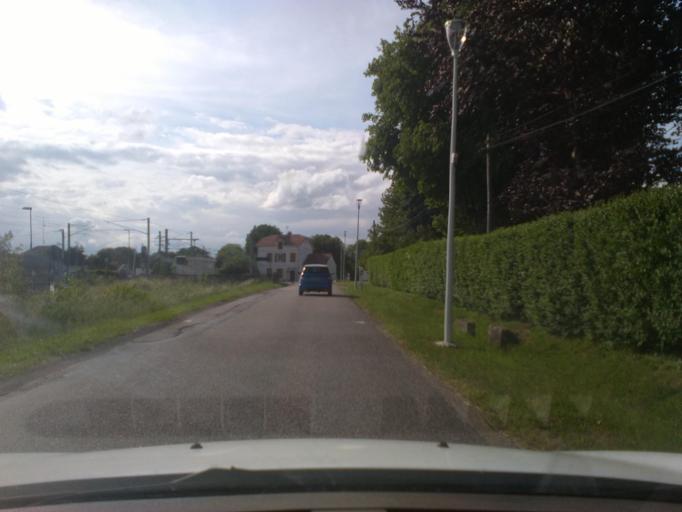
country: FR
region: Lorraine
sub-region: Departement de Meurthe-et-Moselle
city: Baccarat
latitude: 48.4910
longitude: 6.6970
